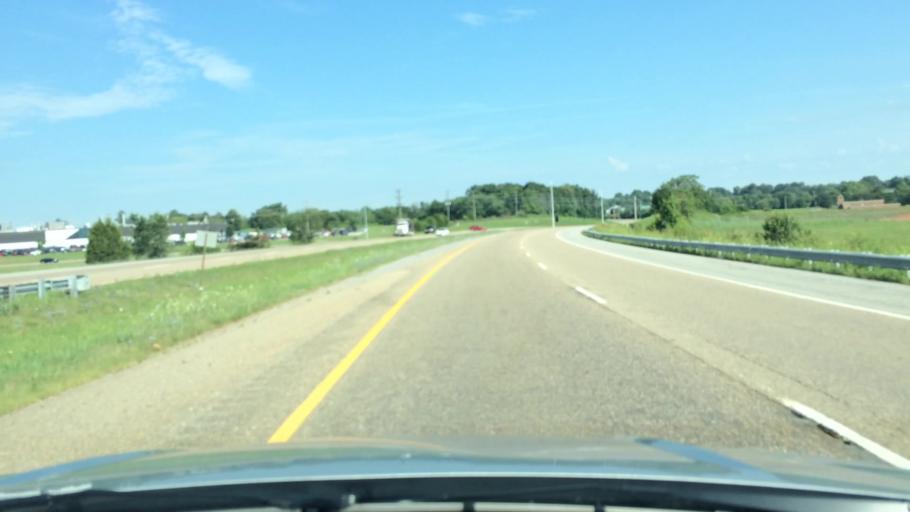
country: US
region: Tennessee
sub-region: Hamblen County
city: Morristown
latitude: 36.1711
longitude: -83.3859
